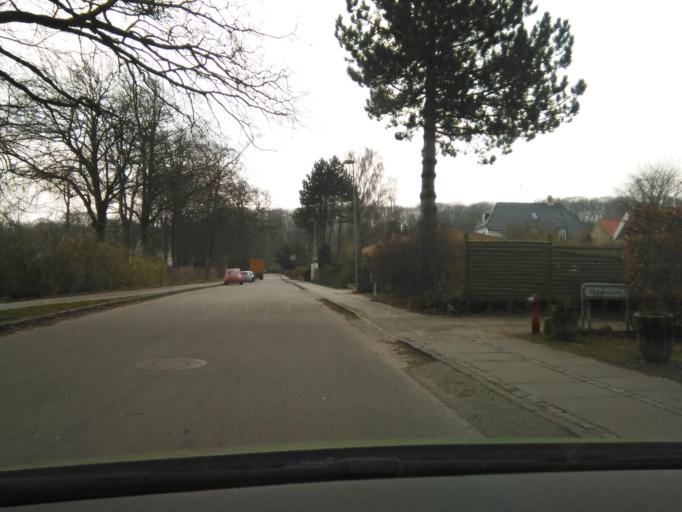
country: DK
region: Central Jutland
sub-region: Arhus Kommune
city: Arhus
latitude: 56.1842
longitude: 10.2289
